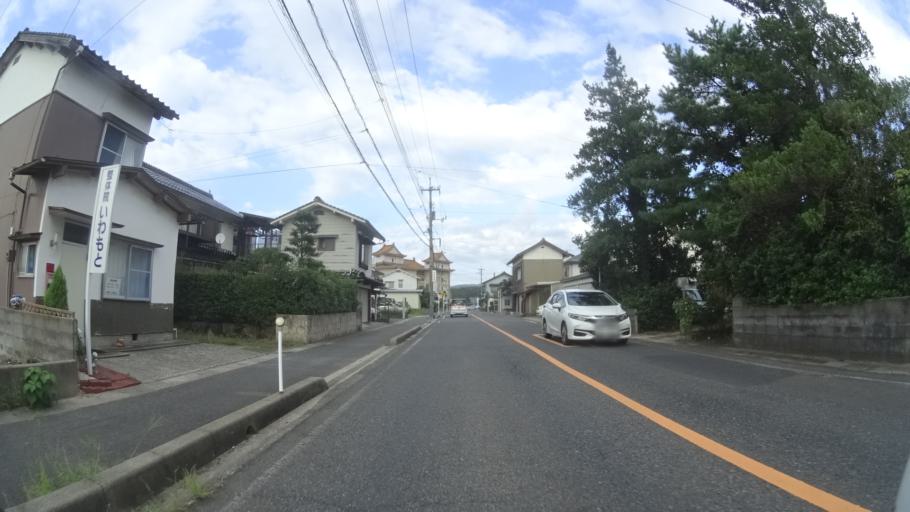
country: JP
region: Tottori
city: Kurayoshi
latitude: 35.4687
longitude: 133.8973
